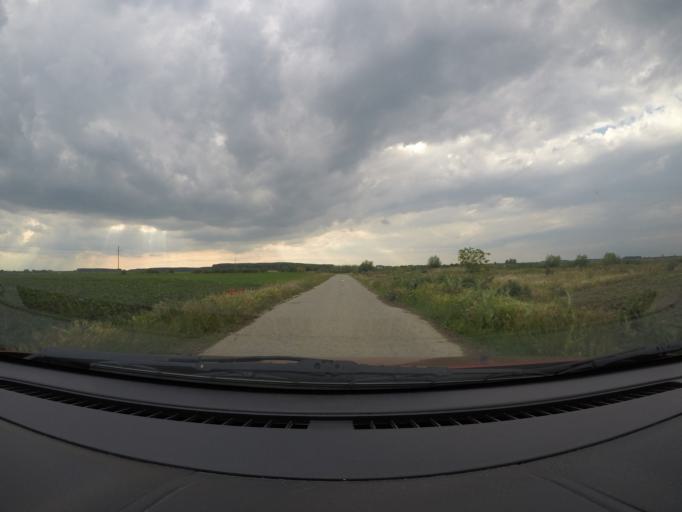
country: RS
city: Uzdin
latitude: 45.2040
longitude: 20.6058
